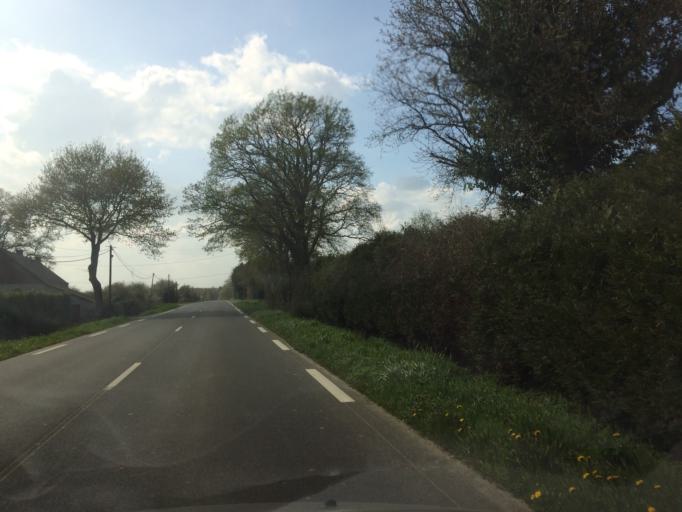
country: FR
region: Pays de la Loire
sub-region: Departement de la Loire-Atlantique
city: Blain
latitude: 47.4835
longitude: -1.8101
